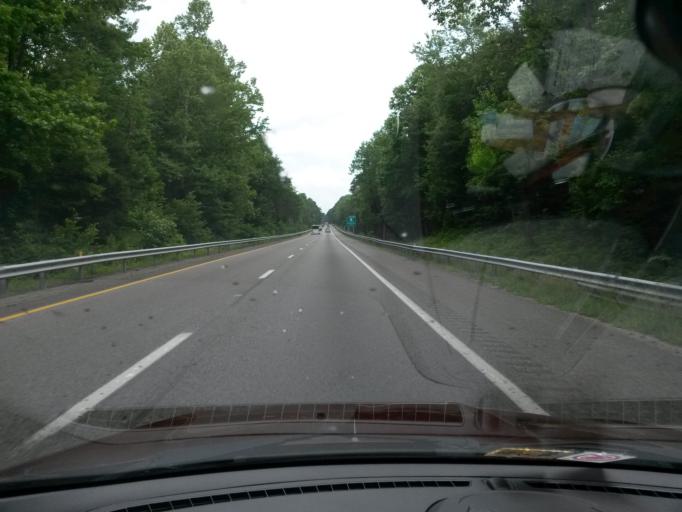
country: US
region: Virginia
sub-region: Goochland County
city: Goochland
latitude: 37.7162
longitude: -77.8041
